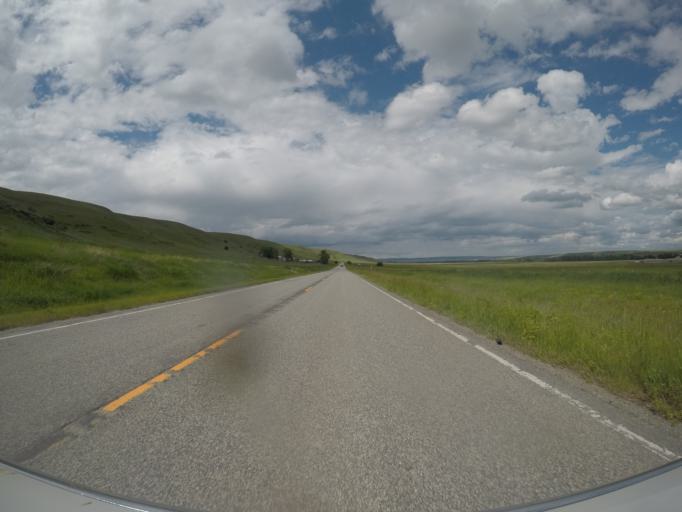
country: US
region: Montana
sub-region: Sweet Grass County
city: Big Timber
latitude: 45.7748
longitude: -109.9879
